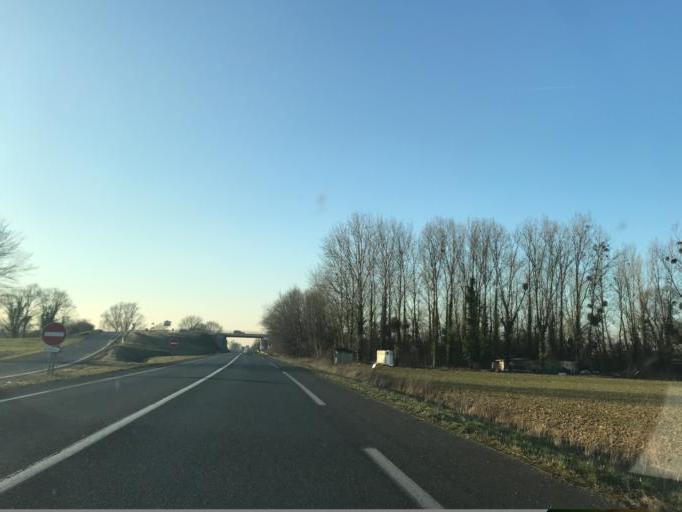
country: FR
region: Ile-de-France
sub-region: Departement de Seine-et-Marne
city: Villiers-sur-Morin
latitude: 48.8547
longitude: 2.8590
